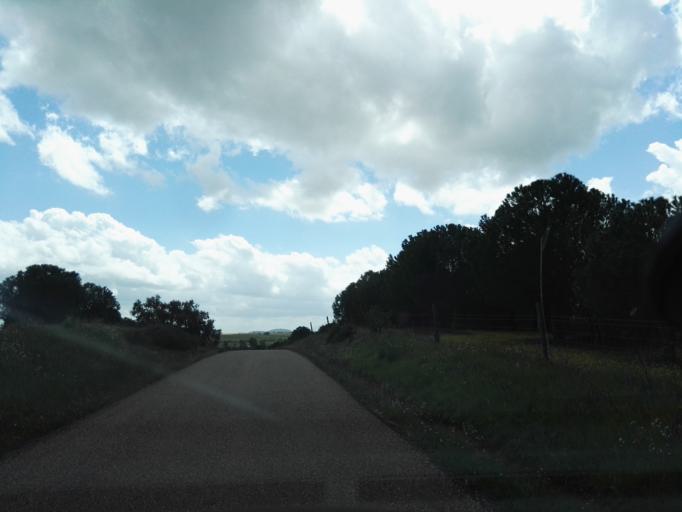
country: PT
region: Portalegre
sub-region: Elvas
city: Elvas
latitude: 38.9798
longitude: -7.1759
